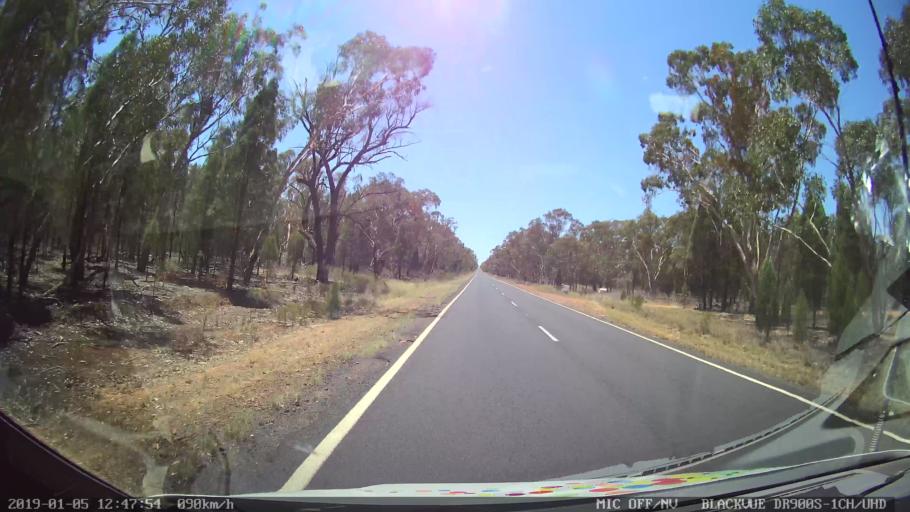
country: AU
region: New South Wales
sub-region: Warrumbungle Shire
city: Coonabarabran
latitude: -31.1182
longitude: 149.5835
